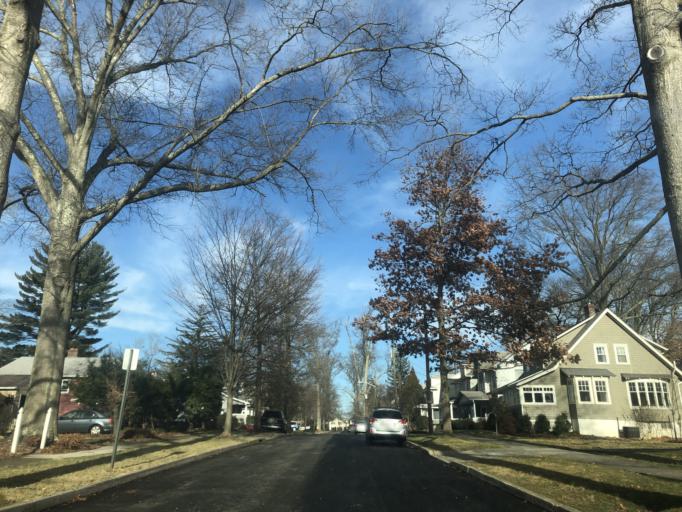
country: US
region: New Jersey
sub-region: Mercer County
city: Princeton
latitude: 40.3529
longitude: -74.6415
